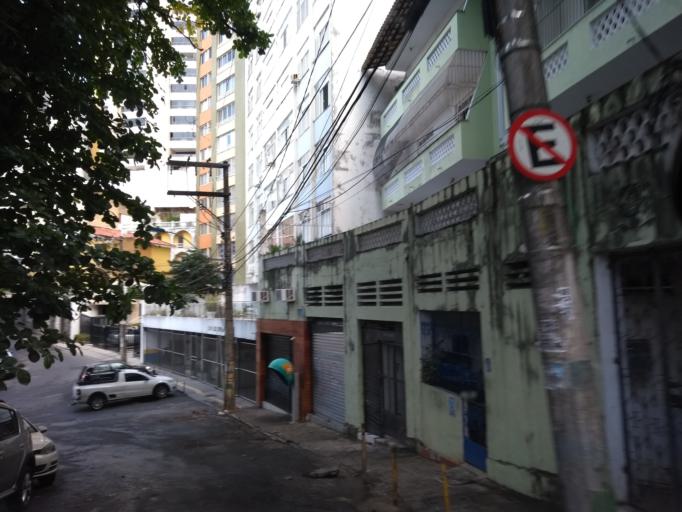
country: BR
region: Bahia
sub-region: Salvador
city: Salvador
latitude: -13.0036
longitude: -38.5255
